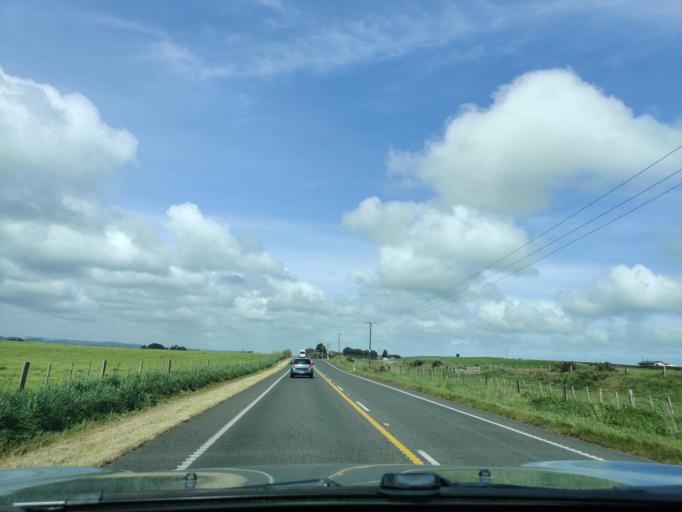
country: NZ
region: Taranaki
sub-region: South Taranaki District
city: Patea
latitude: -39.7749
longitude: 174.6797
